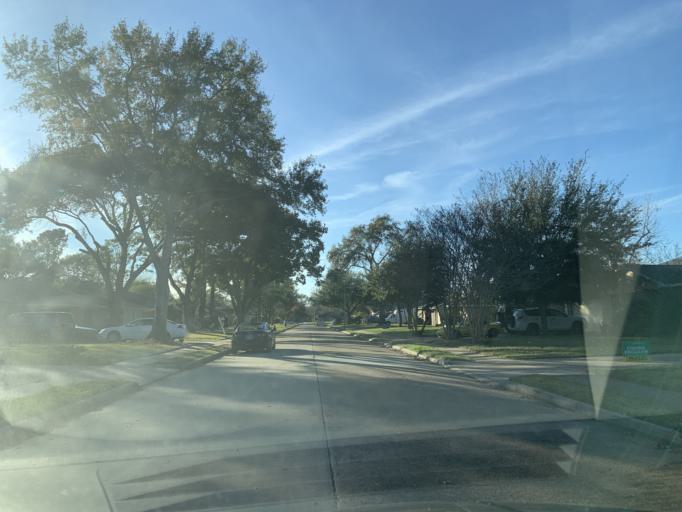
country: US
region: Texas
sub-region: Harris County
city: Bellaire
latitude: 29.6902
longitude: -95.5154
